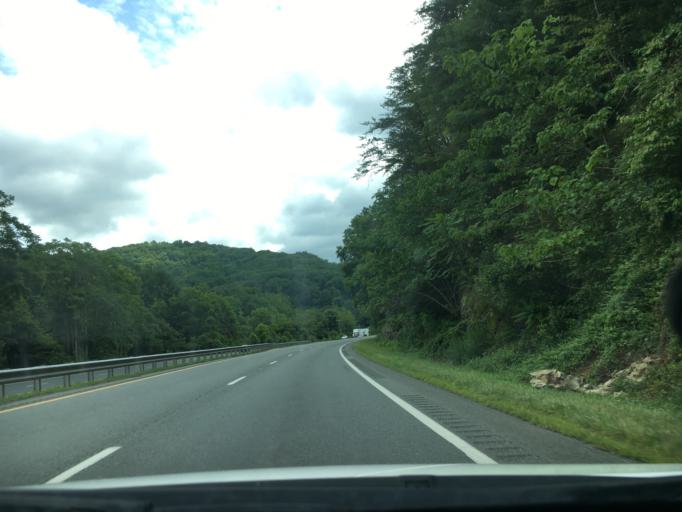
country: US
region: Virginia
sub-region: City of Charlottesville
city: Charlottesville
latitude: 38.0051
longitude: -78.5793
